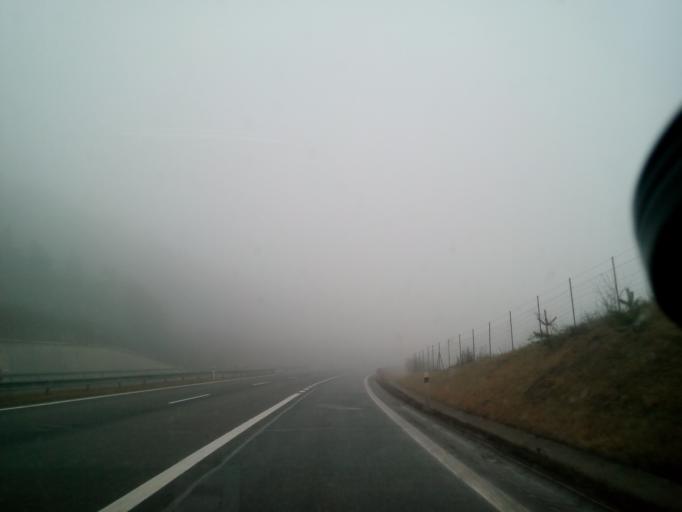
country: SK
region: Kosicky
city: Krompachy
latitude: 49.0126
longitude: 20.9430
